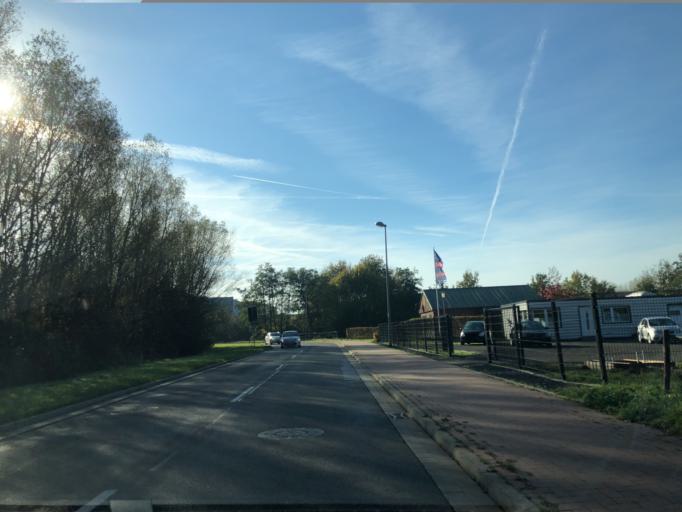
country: DE
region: Lower Saxony
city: Lehe
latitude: 53.0462
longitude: 7.3253
